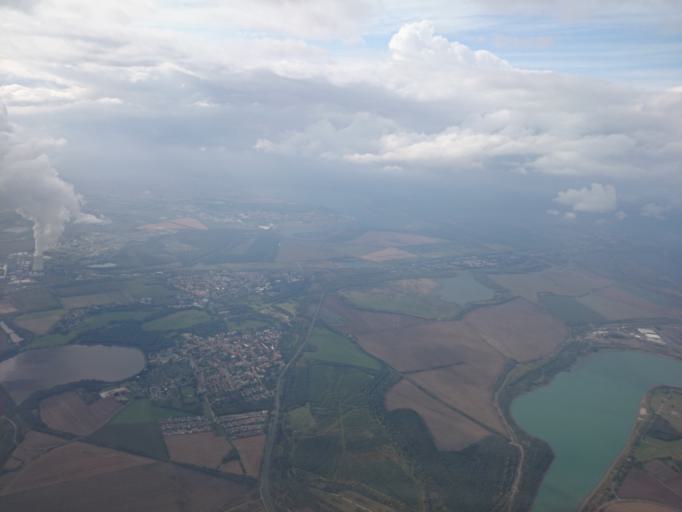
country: DE
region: Saxony
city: Espenhain
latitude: 51.1886
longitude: 12.4735
